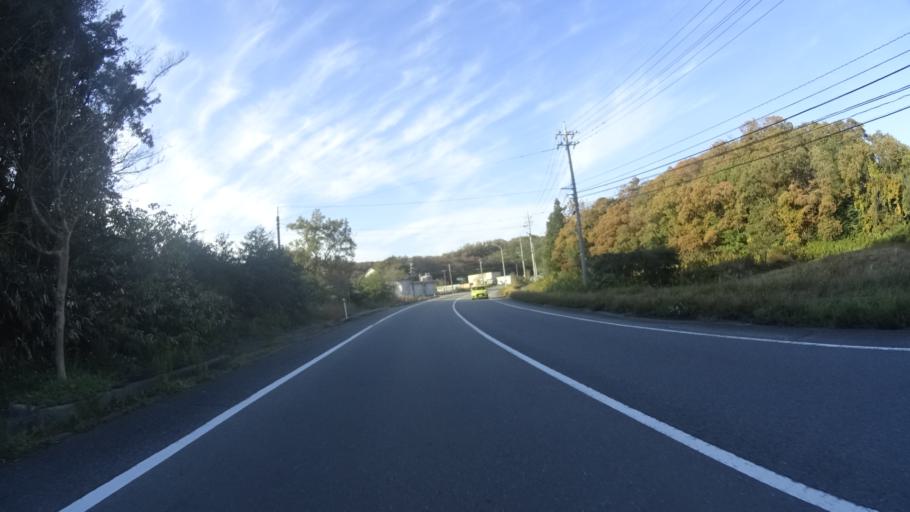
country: JP
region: Ishikawa
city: Hakui
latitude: 37.0277
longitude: 136.7813
